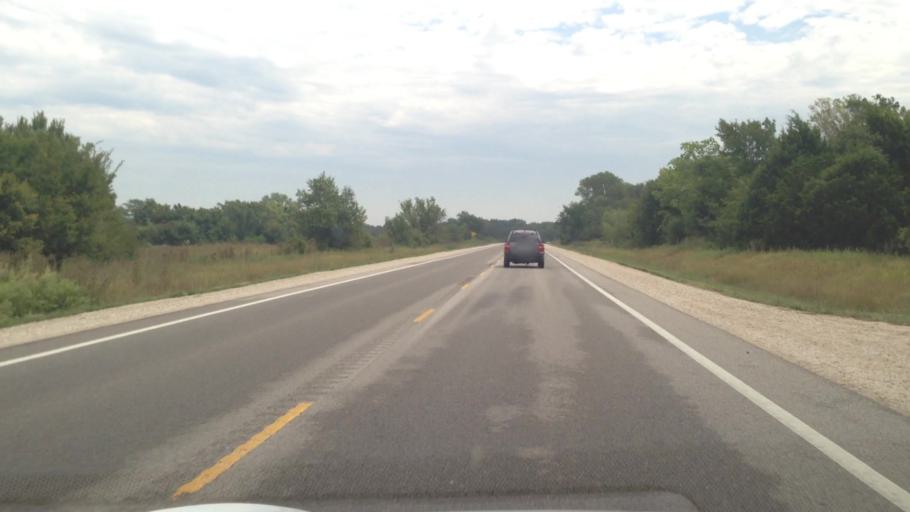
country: US
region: Kansas
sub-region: Allen County
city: Iola
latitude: 37.9145
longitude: -95.1461
